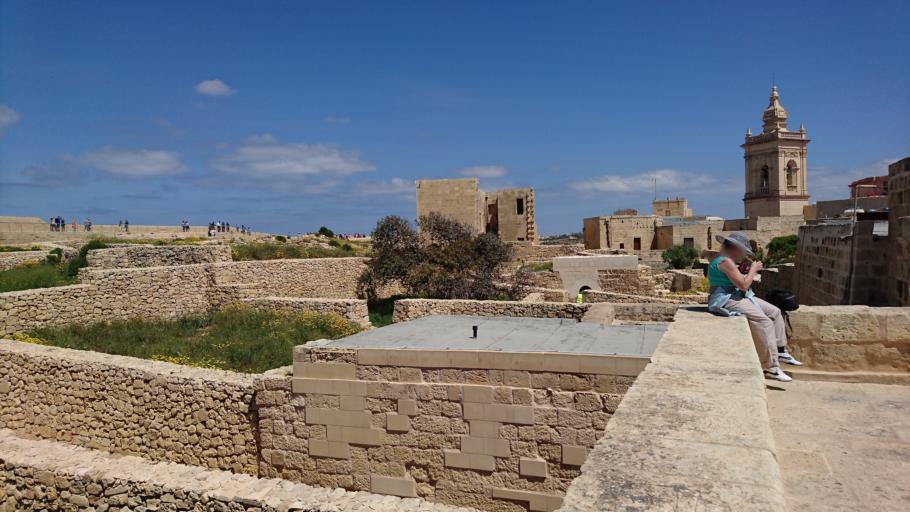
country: MT
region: Victoria
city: Victoria
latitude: 36.0467
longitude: 14.2389
